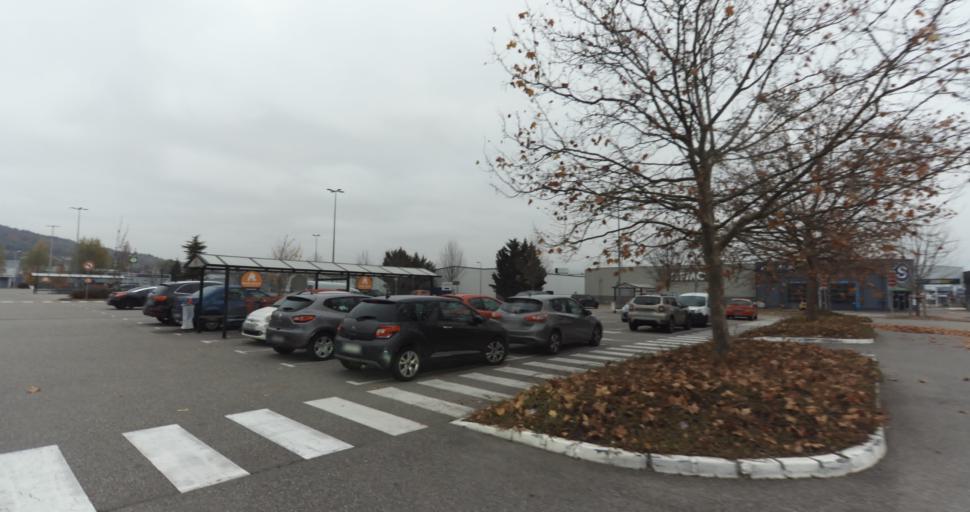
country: FR
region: Rhone-Alpes
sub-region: Departement de la Haute-Savoie
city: Epagny
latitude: 45.9384
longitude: 6.0765
